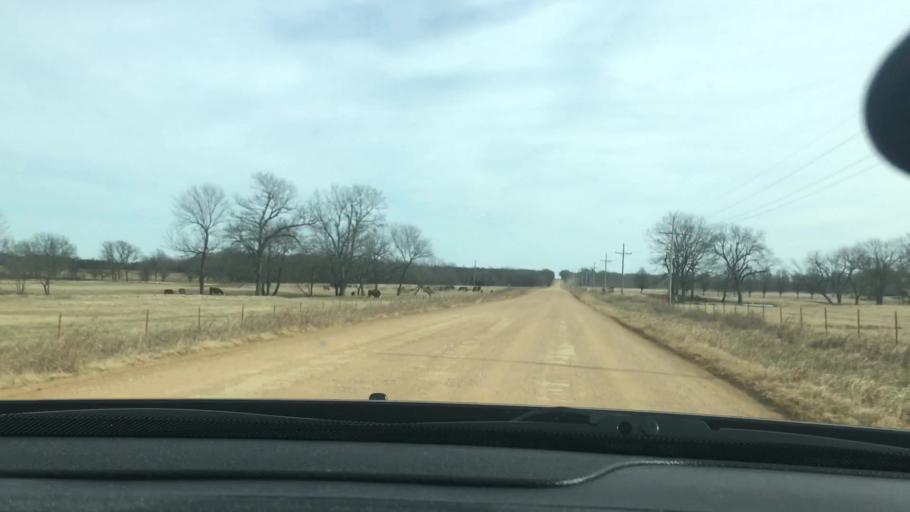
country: US
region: Oklahoma
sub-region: Murray County
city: Sulphur
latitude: 34.4049
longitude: -96.9141
